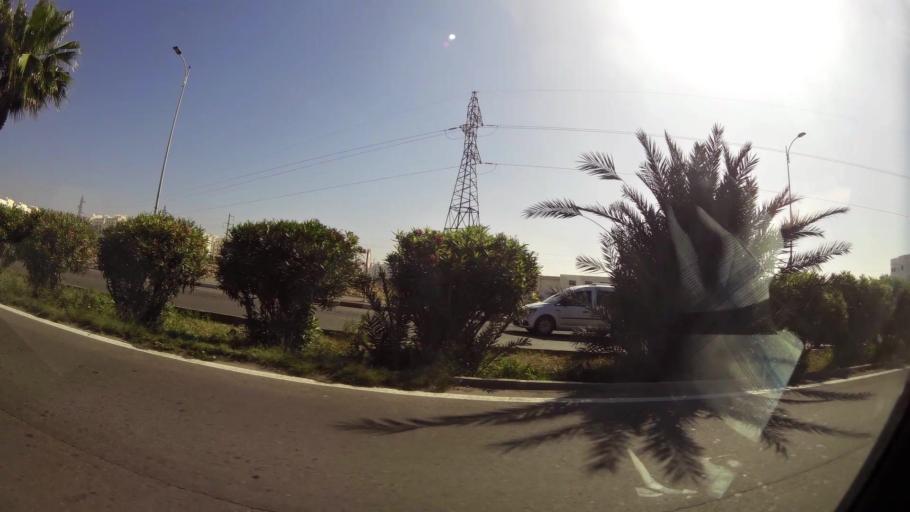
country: MA
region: Souss-Massa-Draa
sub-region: Inezgane-Ait Mellou
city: Inezgane
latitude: 30.3831
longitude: -9.5054
